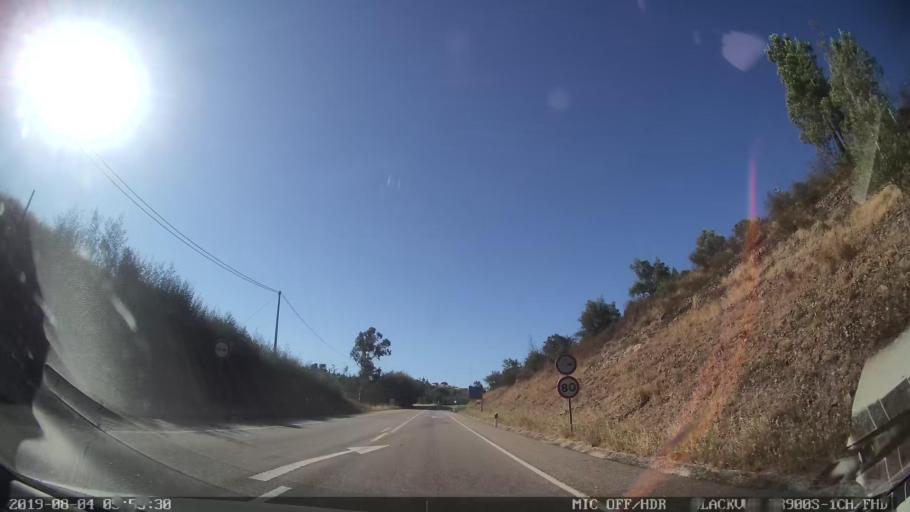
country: PT
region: Portalegre
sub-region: Gaviao
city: Gaviao
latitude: 39.4550
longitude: -7.9299
